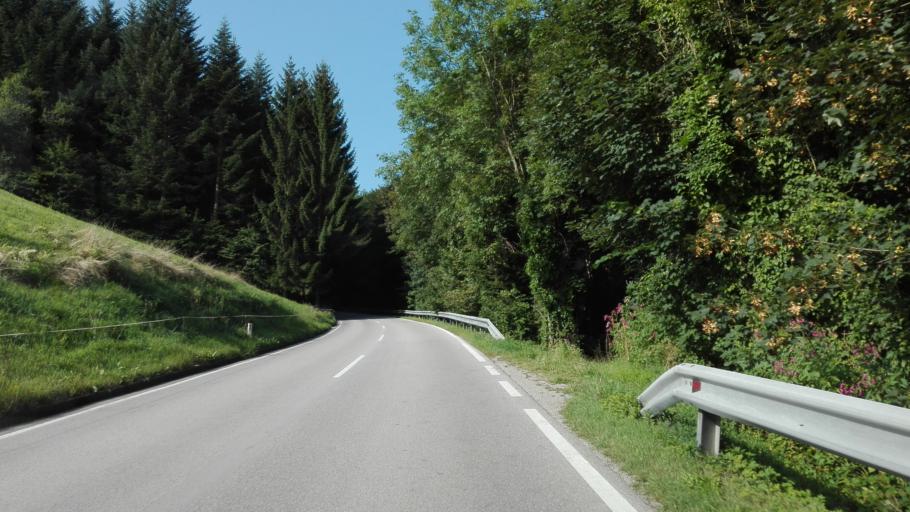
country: AT
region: Lower Austria
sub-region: Politischer Bezirk Lilienfeld
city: Hainfeld
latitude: 48.0818
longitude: 15.7773
